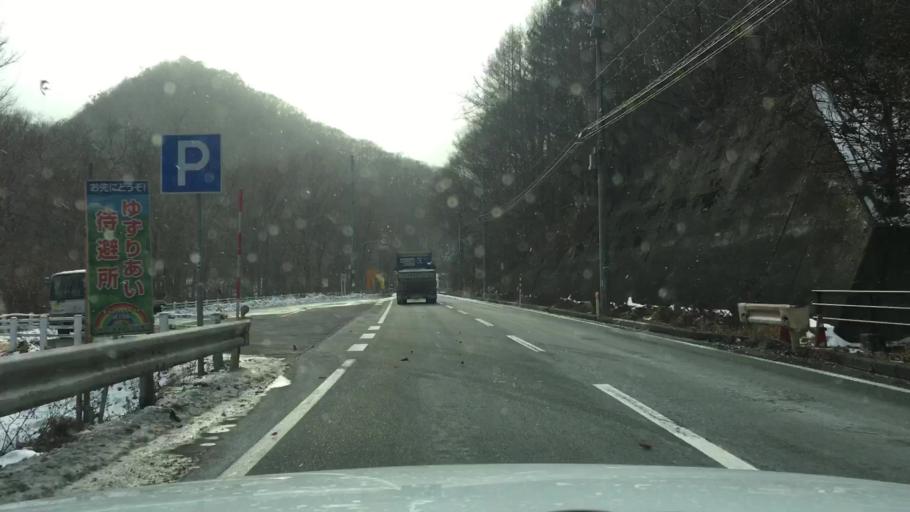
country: JP
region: Iwate
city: Tono
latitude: 39.6181
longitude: 141.4915
